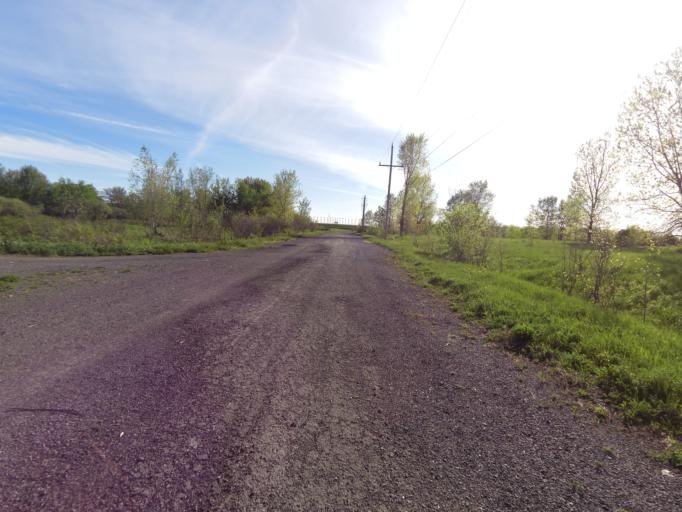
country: CA
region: Ontario
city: Ottawa
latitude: 45.3280
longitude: -75.6386
